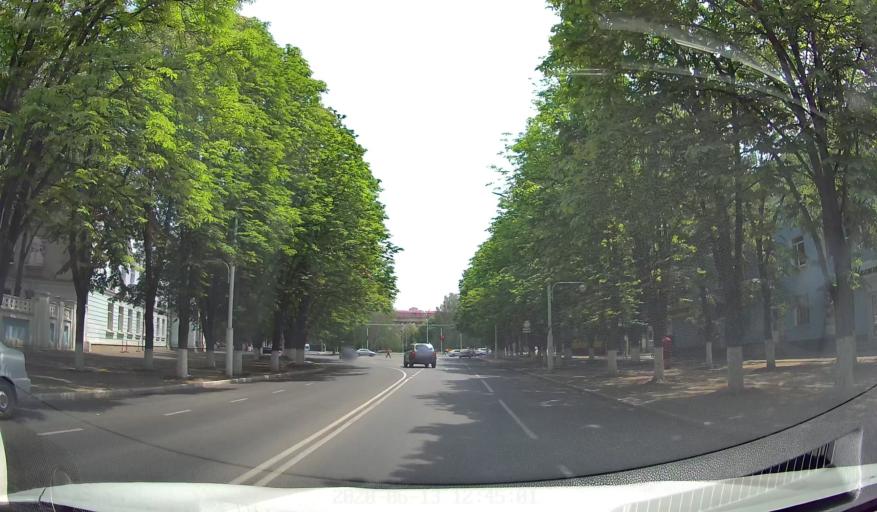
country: GR
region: Attica
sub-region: Nomos Piraios
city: Kythira
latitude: 36.2788
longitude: 23.0640
